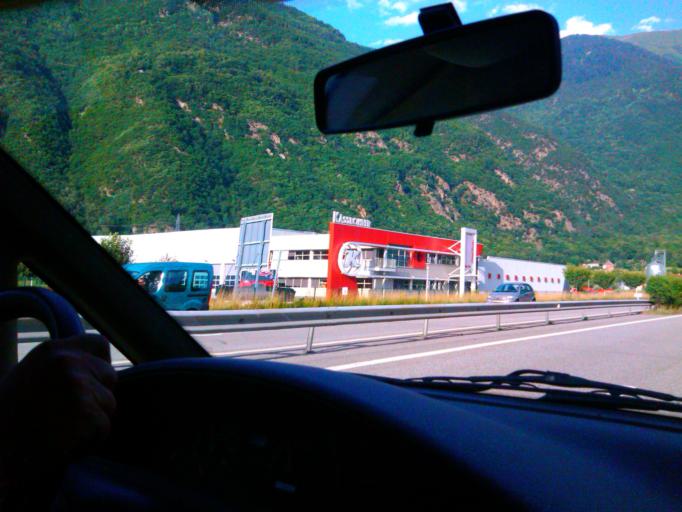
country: FR
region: Rhone-Alpes
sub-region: Departement de la Savoie
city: Albertville
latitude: 45.6590
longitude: 6.4260
